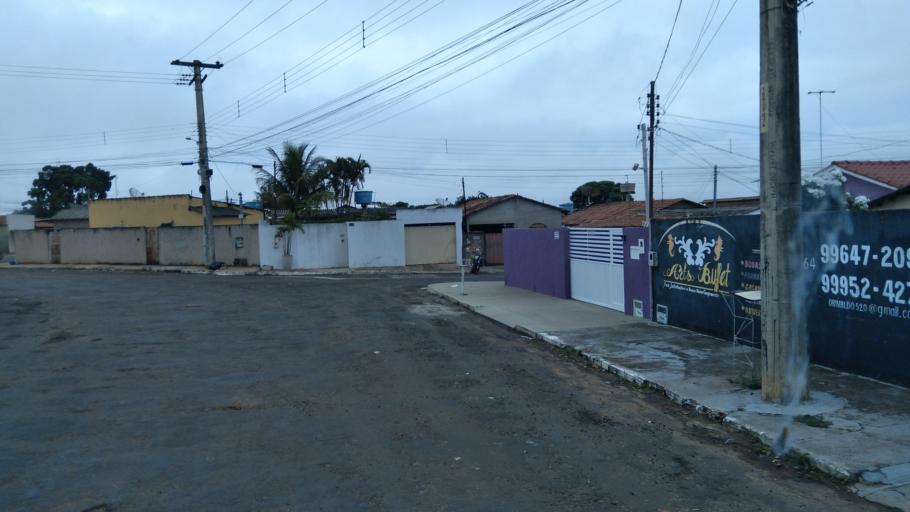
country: BR
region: Goias
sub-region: Mineiros
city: Mineiros
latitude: -17.5727
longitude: -52.5381
